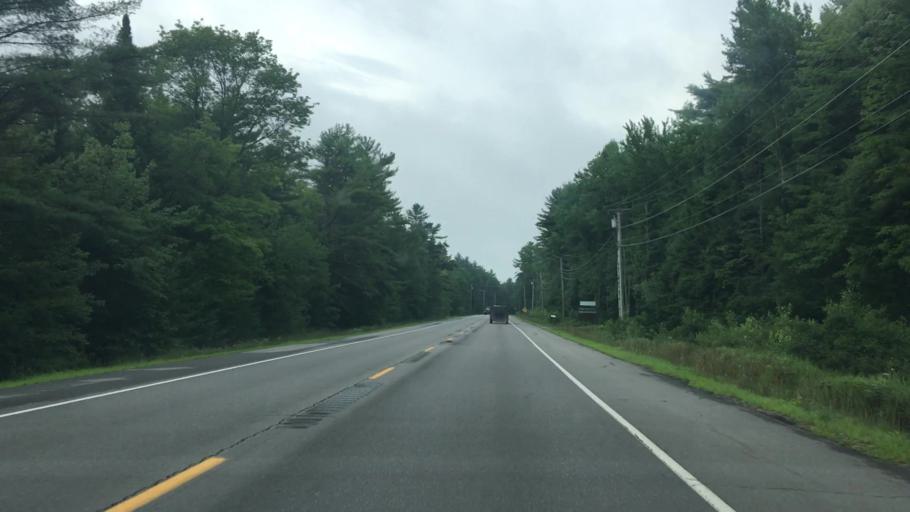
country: US
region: Maine
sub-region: York County
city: Lebanon
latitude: 43.3866
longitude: -70.8765
